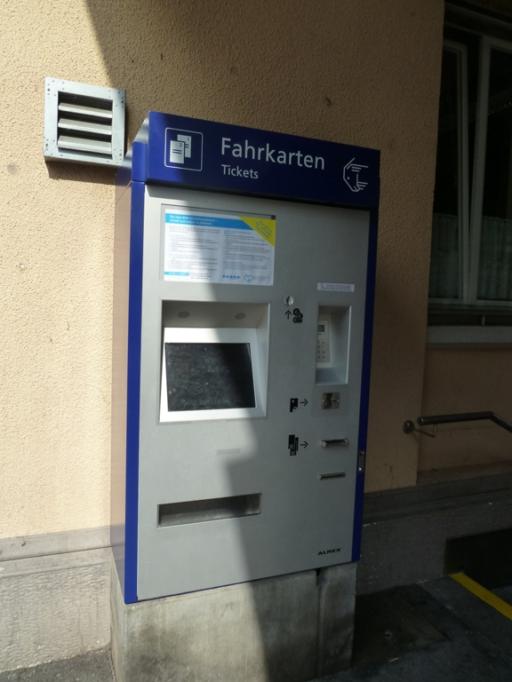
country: DE
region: Baden-Wuerttemberg
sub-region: Tuebingen Region
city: Friedrichshafen
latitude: 47.6529
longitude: 9.4739
